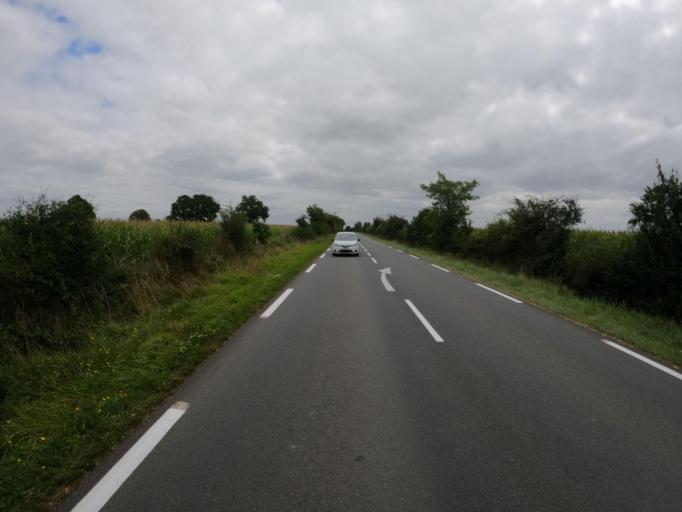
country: FR
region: Poitou-Charentes
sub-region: Departement de la Vienne
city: Availles-Limouzine
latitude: 46.1178
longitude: 0.5417
